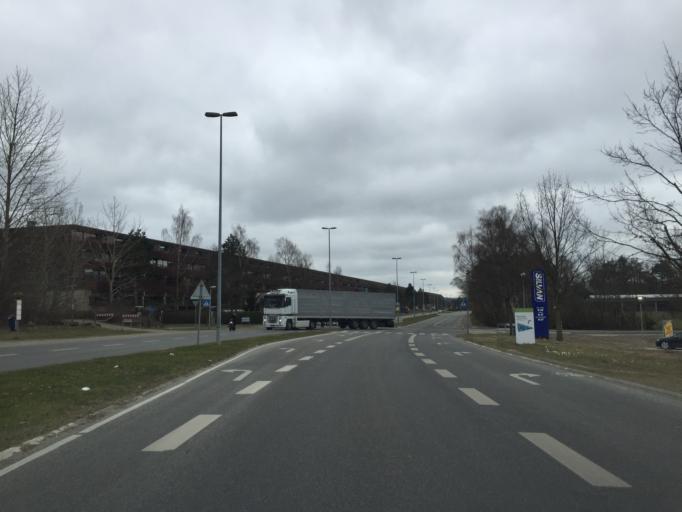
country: DK
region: Capital Region
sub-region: Fureso Kommune
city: Farum
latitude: 55.8225
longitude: 12.3745
